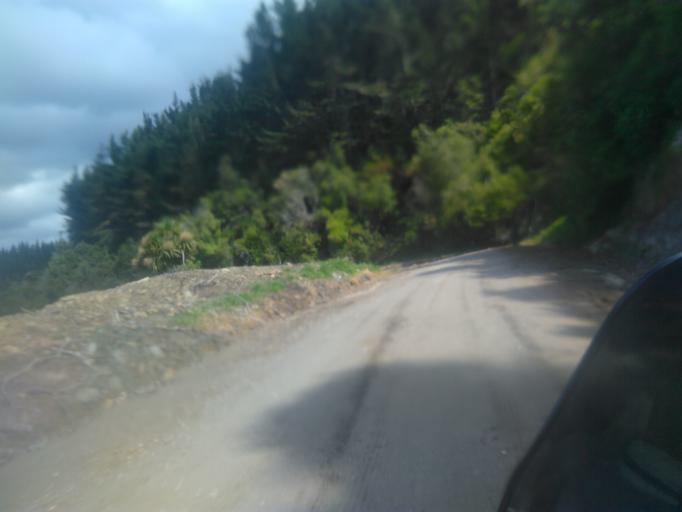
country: NZ
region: Hawke's Bay
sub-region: Wairoa District
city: Wairoa
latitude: -38.7719
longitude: 177.6044
